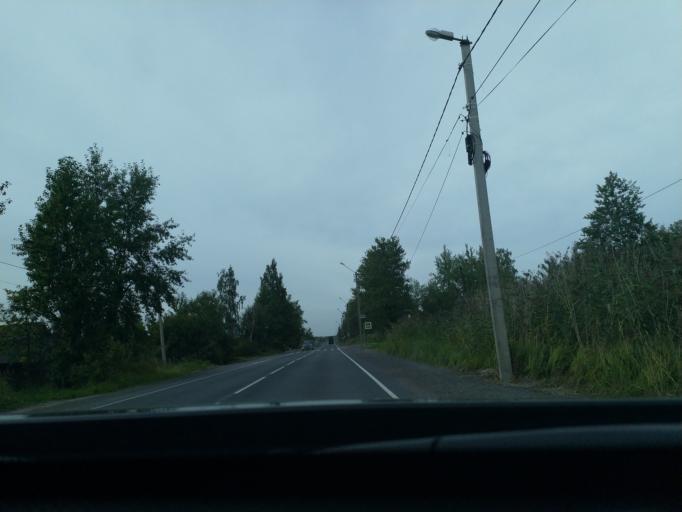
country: RU
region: Leningrad
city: Nikol'skoye
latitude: 59.7156
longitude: 30.7792
